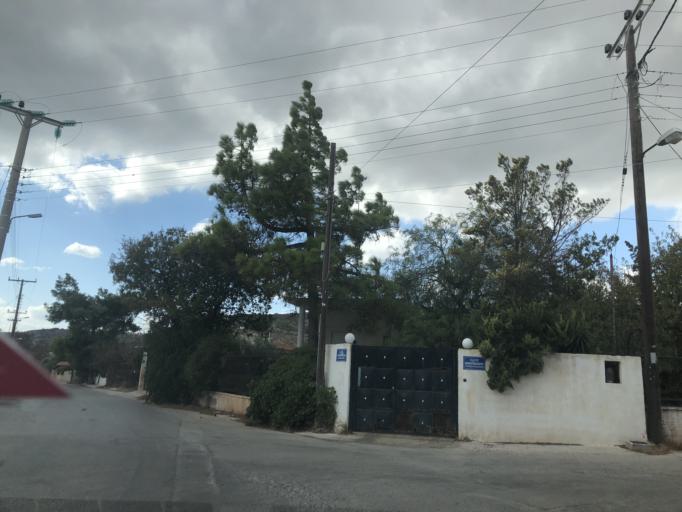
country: GR
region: Attica
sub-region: Nomarchia Anatolikis Attikis
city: Agia Marina
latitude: 37.8213
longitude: 23.8445
